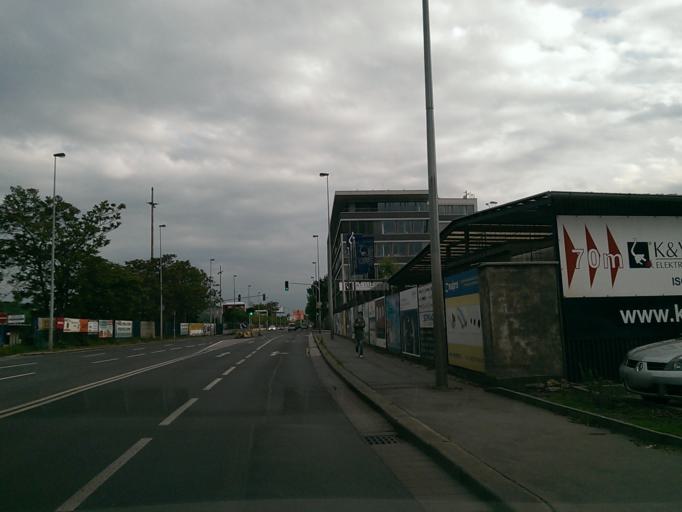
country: CZ
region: Praha
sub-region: Praha 2
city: Vysehrad
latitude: 50.0610
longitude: 14.4111
